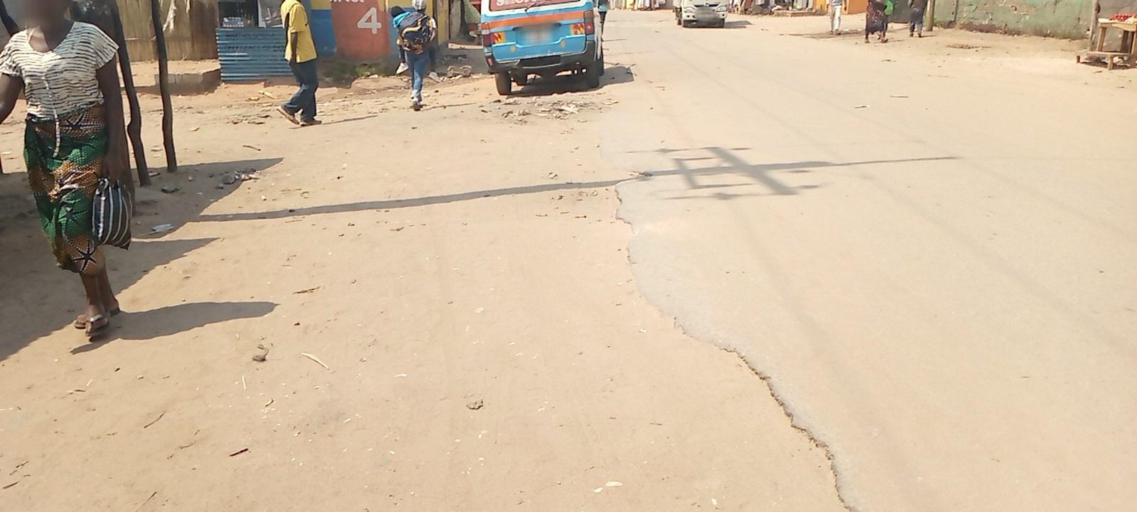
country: ZM
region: Lusaka
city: Lusaka
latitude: -15.4054
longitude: 28.3561
